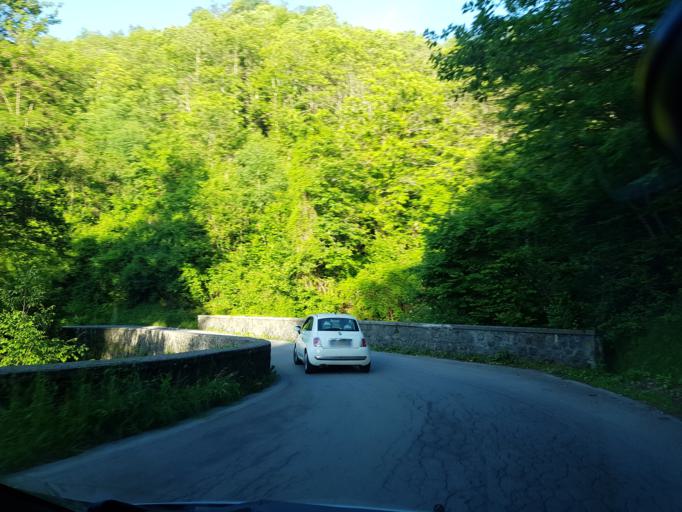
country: IT
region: Tuscany
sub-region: Provincia di Lucca
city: Minucciano
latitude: 44.1782
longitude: 10.2017
